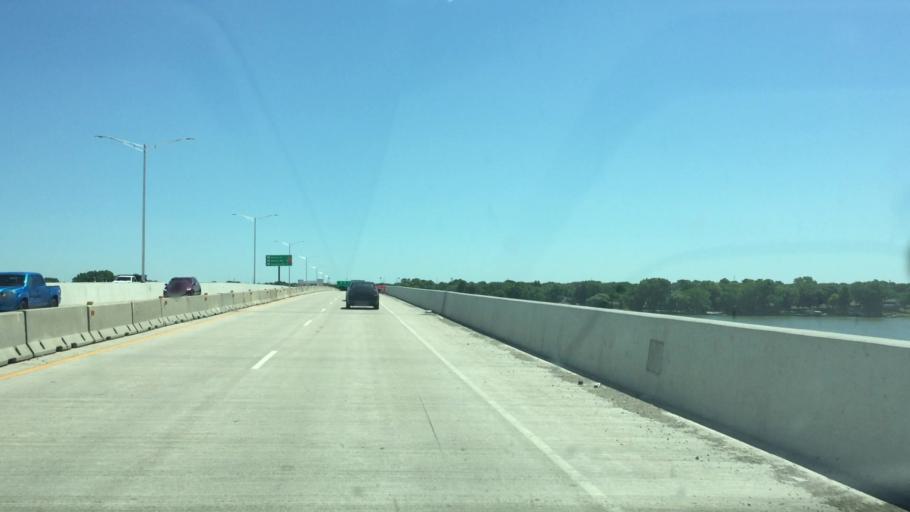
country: US
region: Wisconsin
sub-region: Winnebago County
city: Menasha
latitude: 44.2180
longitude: -88.4634
